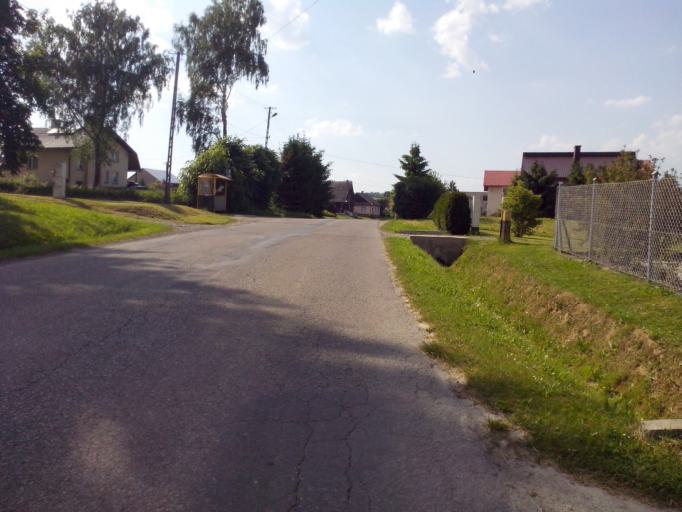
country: PL
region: Subcarpathian Voivodeship
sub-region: Powiat brzozowski
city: Blizne
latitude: 49.7345
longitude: 21.9817
